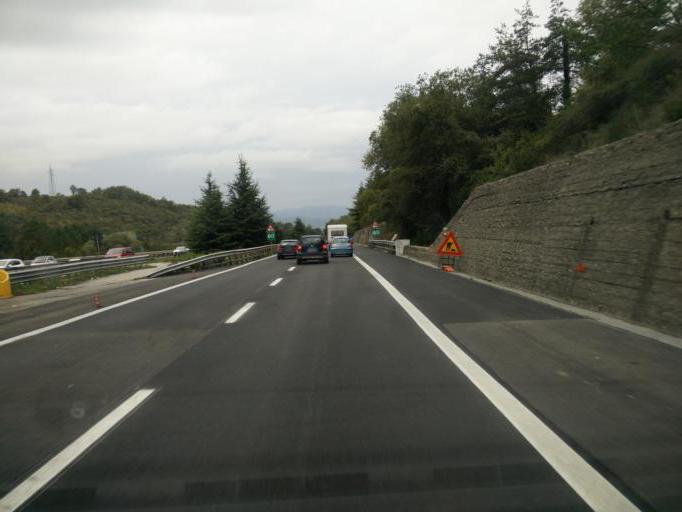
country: IT
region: Tuscany
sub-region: Province of Florence
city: Cavallina
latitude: 43.9481
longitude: 11.2139
